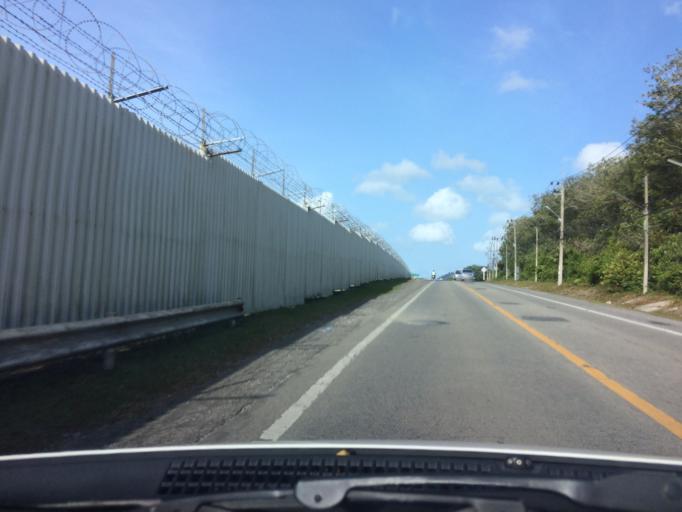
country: TH
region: Phuket
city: Thalang
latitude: 8.1126
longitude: 98.3290
